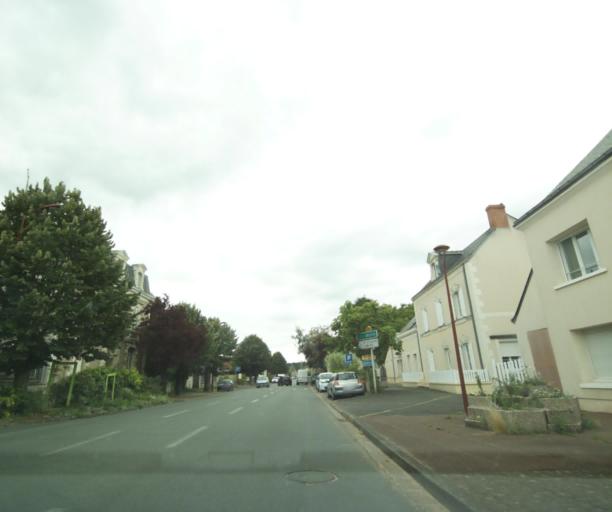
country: FR
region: Pays de la Loire
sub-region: Departement de Maine-et-Loire
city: Pellouailles-les-Vignes
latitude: 47.5218
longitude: -0.4358
